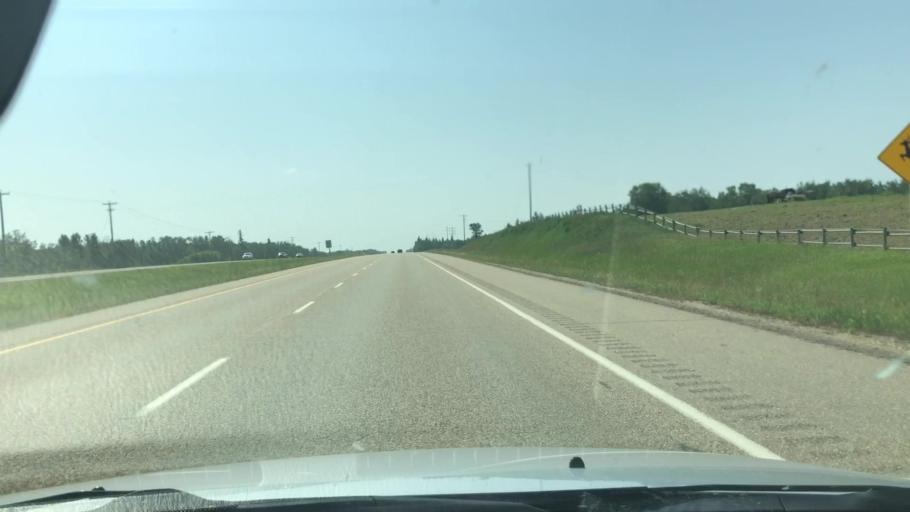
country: CA
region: Alberta
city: Devon
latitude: 53.4406
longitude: -113.7628
